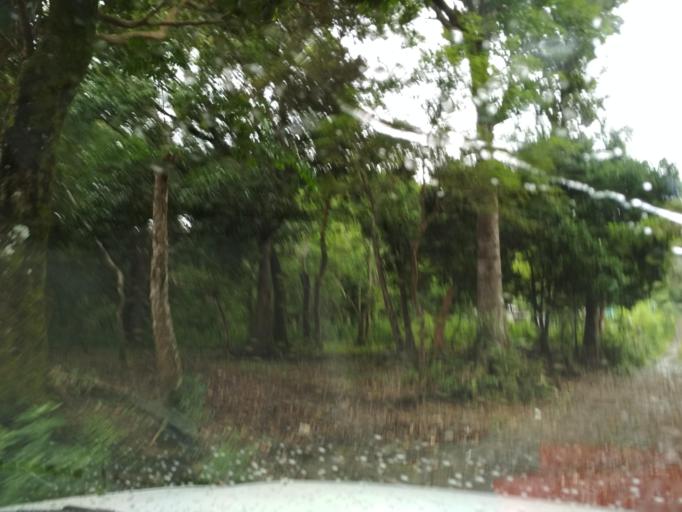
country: MX
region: Veracruz
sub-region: San Andres Tuxtla
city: San Isidro Xoteapan (San Isidro Texcaltitan)
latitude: 18.4626
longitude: -95.2356
